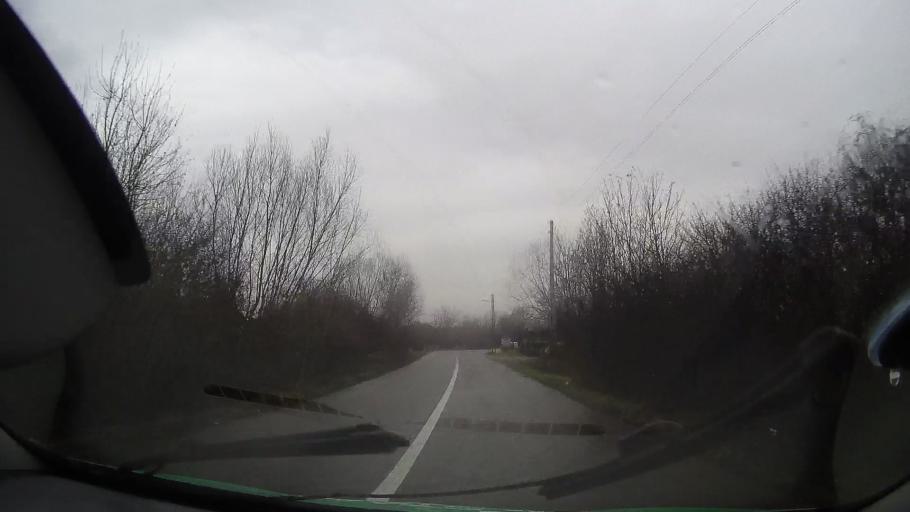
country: RO
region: Bihor
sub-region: Comuna Tinca
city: Tinca
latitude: 46.7414
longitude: 21.9540
